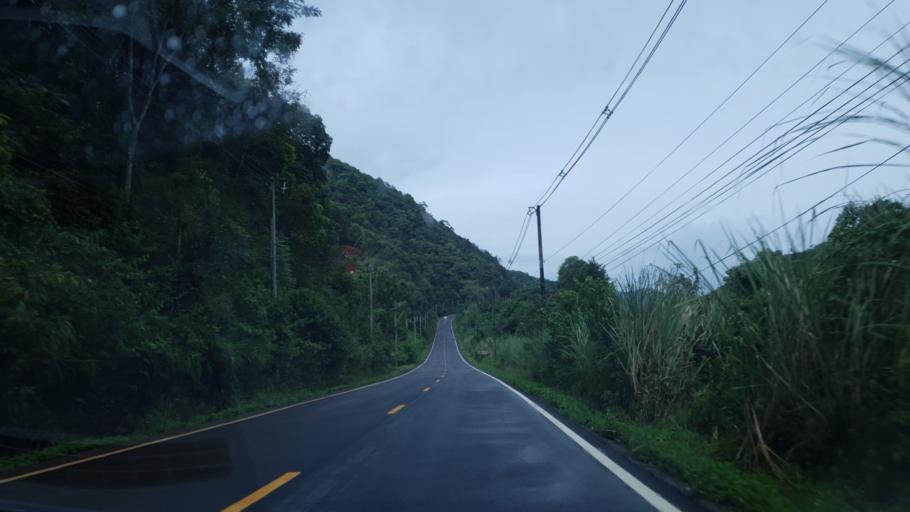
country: TH
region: Mae Hong Son
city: Ban Huai I Huak
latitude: 18.1470
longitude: 98.1000
